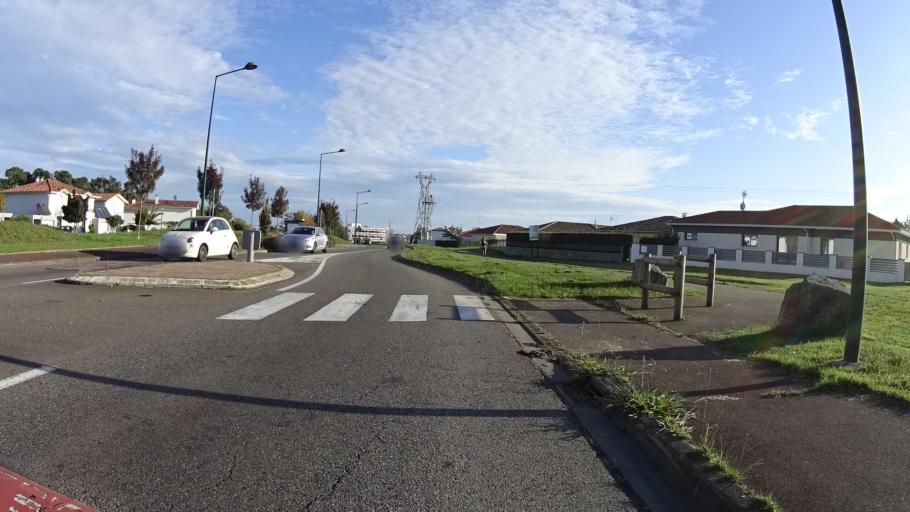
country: FR
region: Aquitaine
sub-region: Departement des Landes
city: Saint-Paul-les-Dax
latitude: 43.7347
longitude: -1.0476
